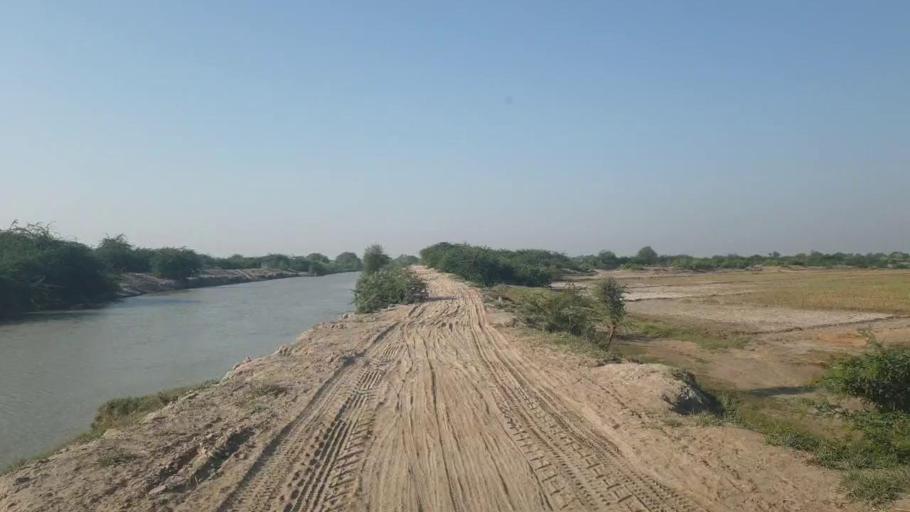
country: PK
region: Sindh
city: Tando Bago
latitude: 24.7233
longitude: 68.9207
